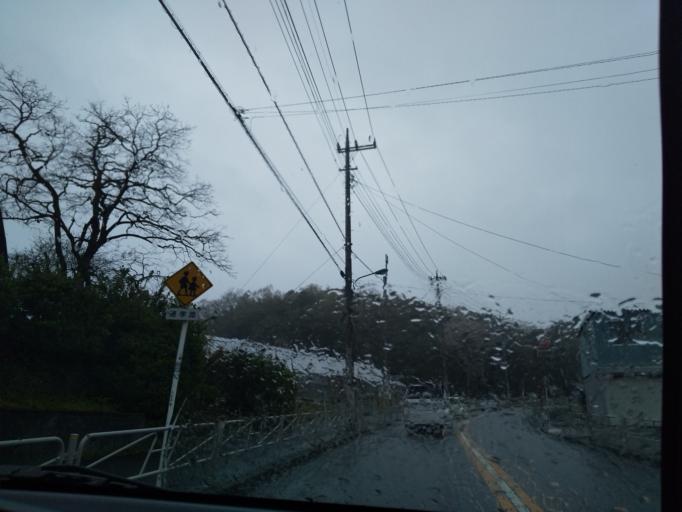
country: JP
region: Tokyo
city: Hino
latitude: 35.6371
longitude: 139.4045
